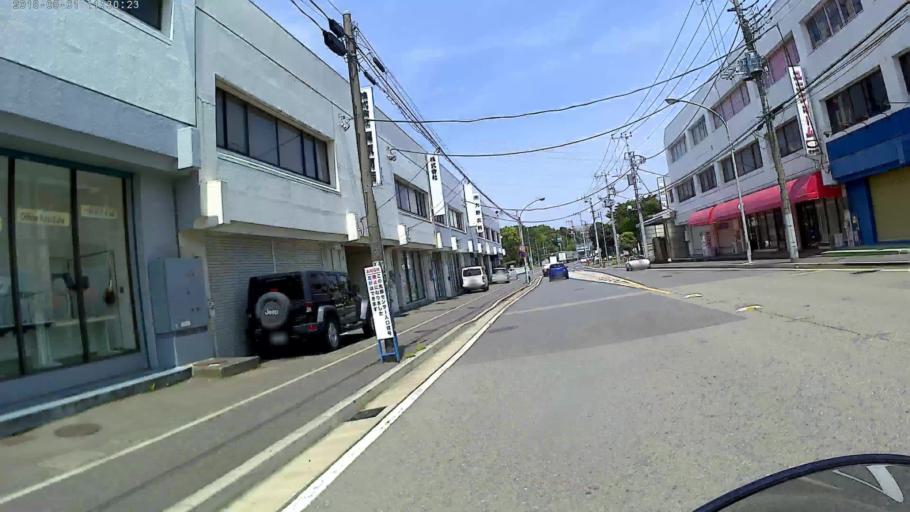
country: JP
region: Kanagawa
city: Minami-rinkan
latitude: 35.5010
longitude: 139.4862
